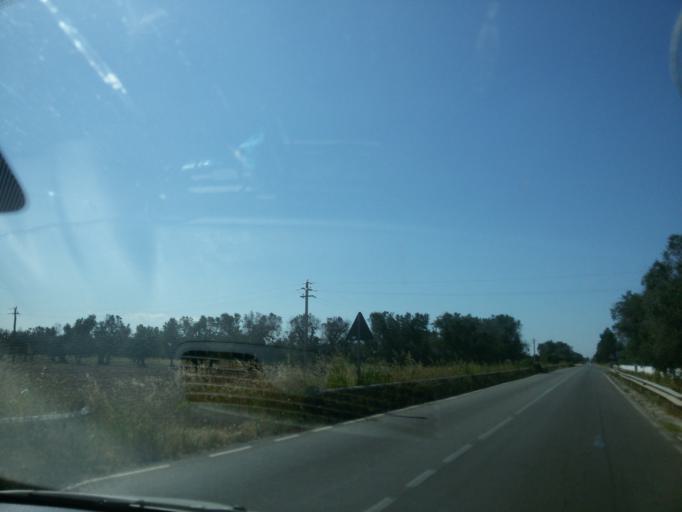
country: IT
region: Apulia
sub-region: Provincia di Brindisi
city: San Donaci
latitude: 40.4580
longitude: 17.9126
